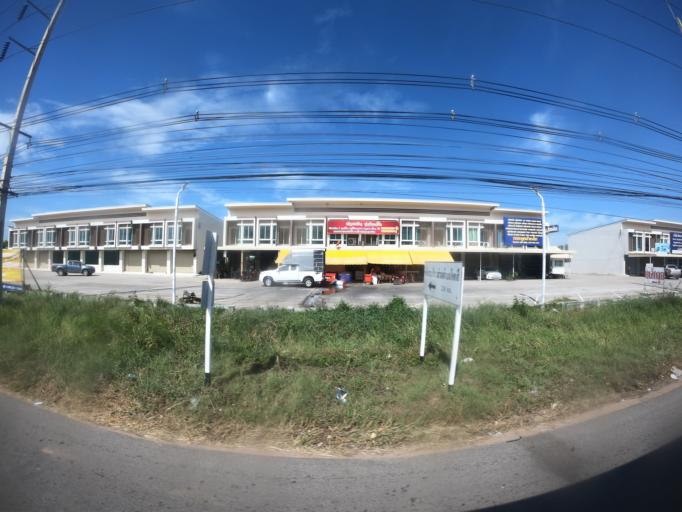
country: TH
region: Khon Kaen
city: Khon Kaen
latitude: 16.4443
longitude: 102.9470
